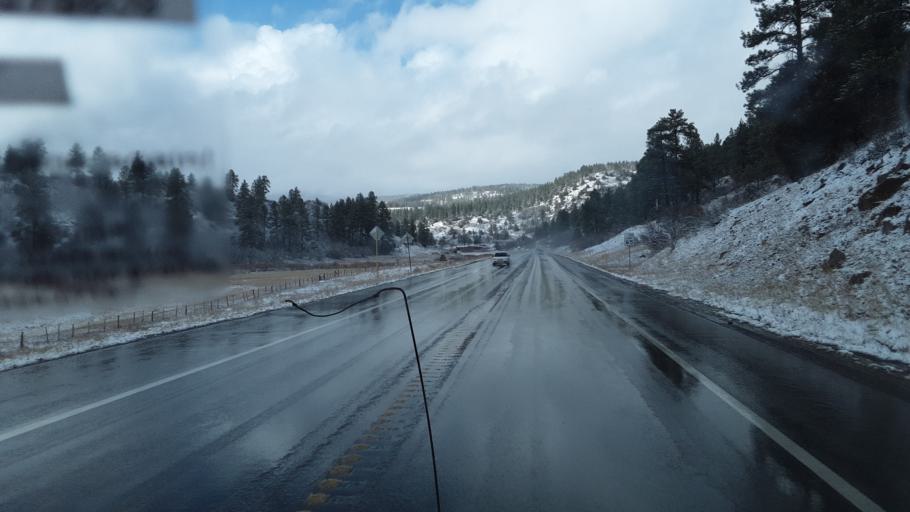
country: US
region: Colorado
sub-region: Archuleta County
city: Pagosa Springs
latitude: 37.2321
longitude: -107.1260
